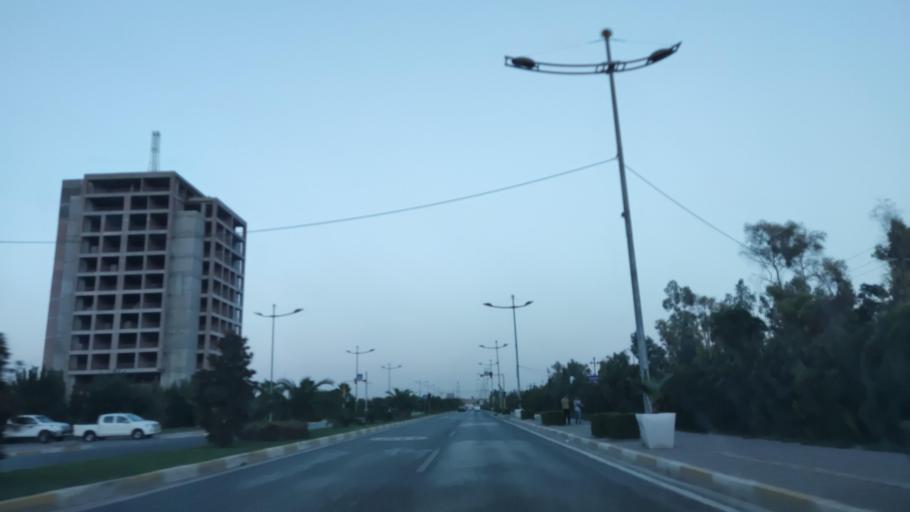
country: IQ
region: Arbil
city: Erbil
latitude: 36.1984
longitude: 43.9849
